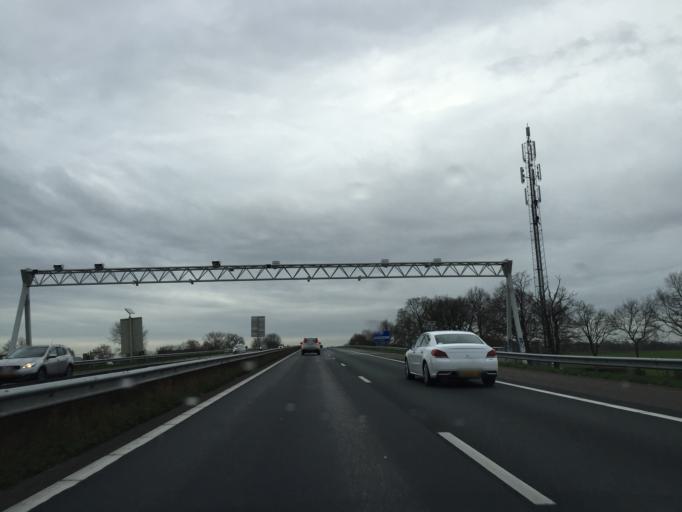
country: NL
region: North Brabant
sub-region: Roosendaal
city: Roosendaal
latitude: 51.5195
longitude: 4.4213
